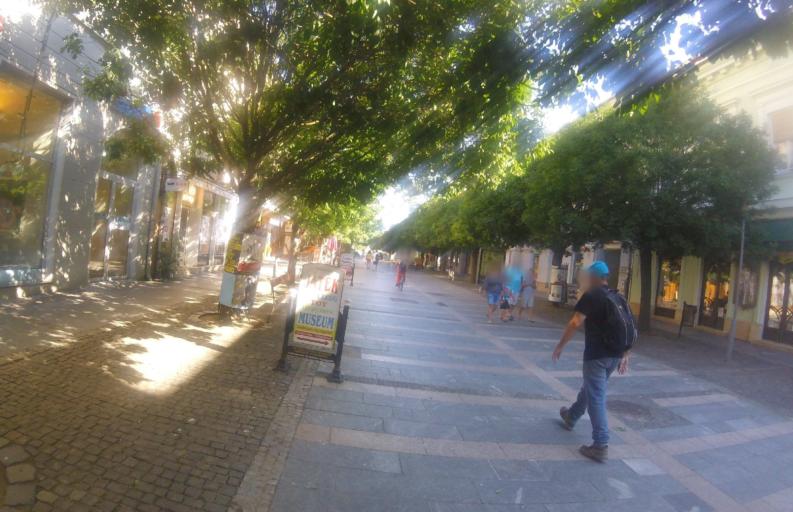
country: HU
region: Zala
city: Keszthely
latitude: 46.7675
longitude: 17.2425
